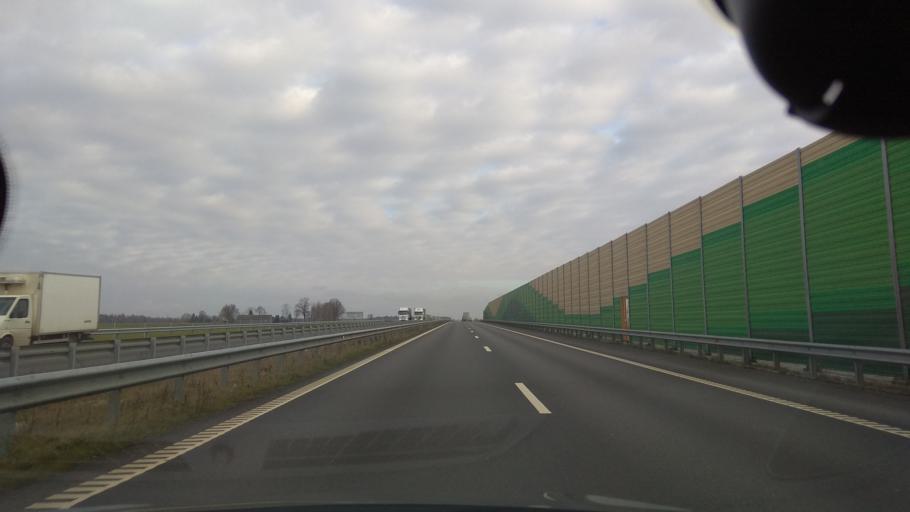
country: LT
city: Kazlu Ruda
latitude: 54.6445
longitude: 23.4848
